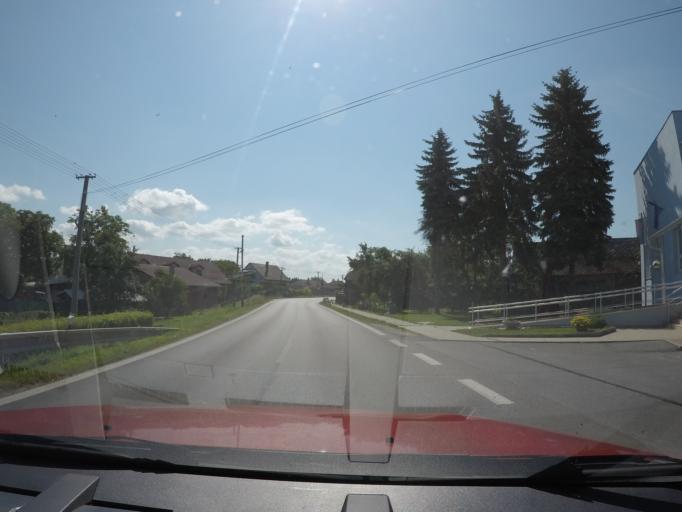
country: SK
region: Presovsky
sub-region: Okres Presov
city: Presov
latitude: 48.9009
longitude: 21.2412
